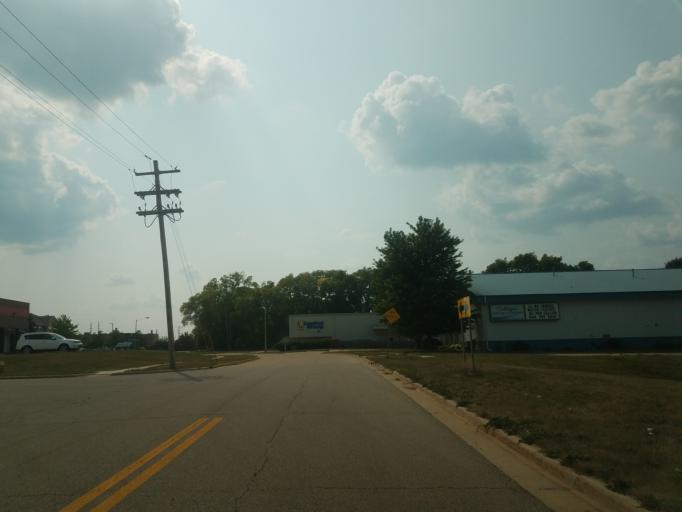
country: US
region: Illinois
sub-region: McLean County
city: Bloomington
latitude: 40.4609
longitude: -88.9755
